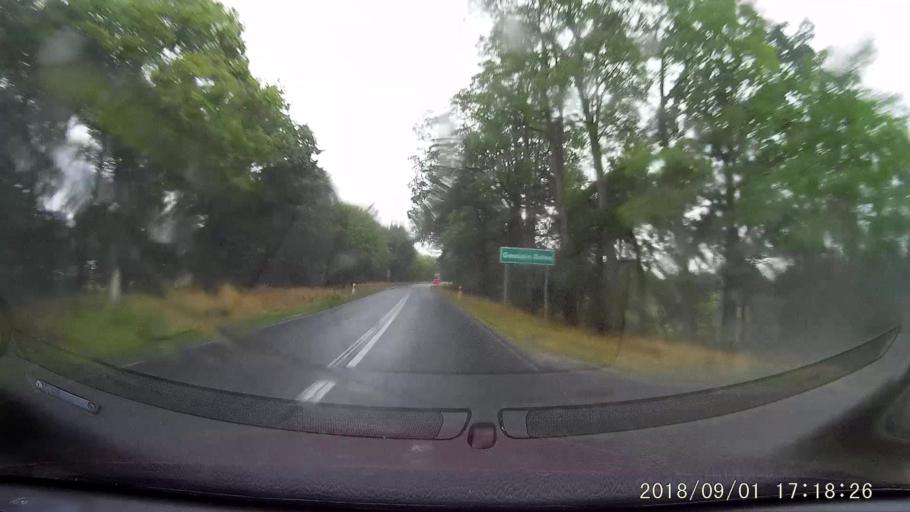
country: PL
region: Lubusz
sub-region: Powiat zielonogorski
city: Nowogrod Bobrzanski
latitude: 51.7389
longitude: 15.2706
